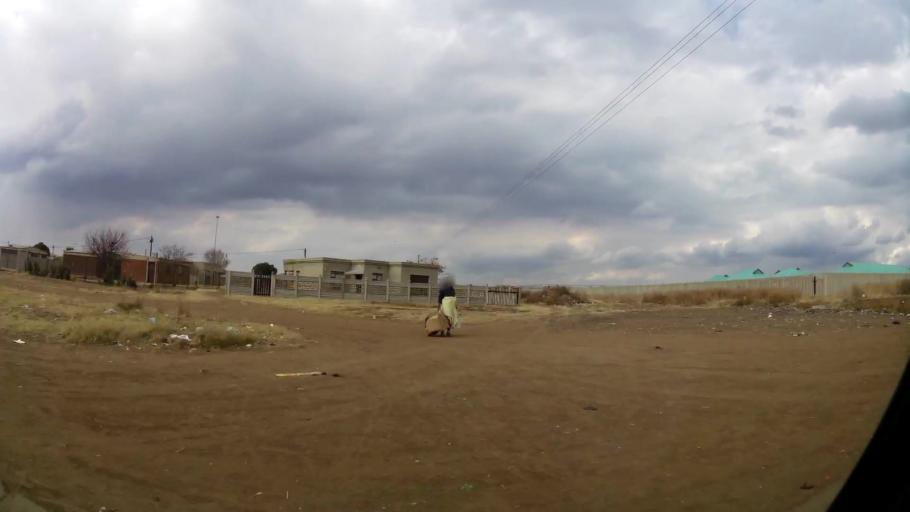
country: ZA
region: Gauteng
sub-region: Sedibeng District Municipality
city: Vanderbijlpark
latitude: -26.6899
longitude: 27.7843
